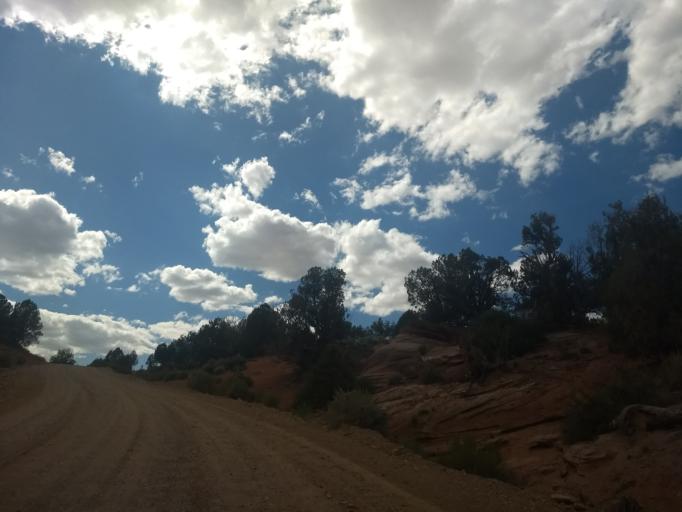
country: US
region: Utah
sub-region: Kane County
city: Kanab
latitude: 37.1521
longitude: -112.5420
